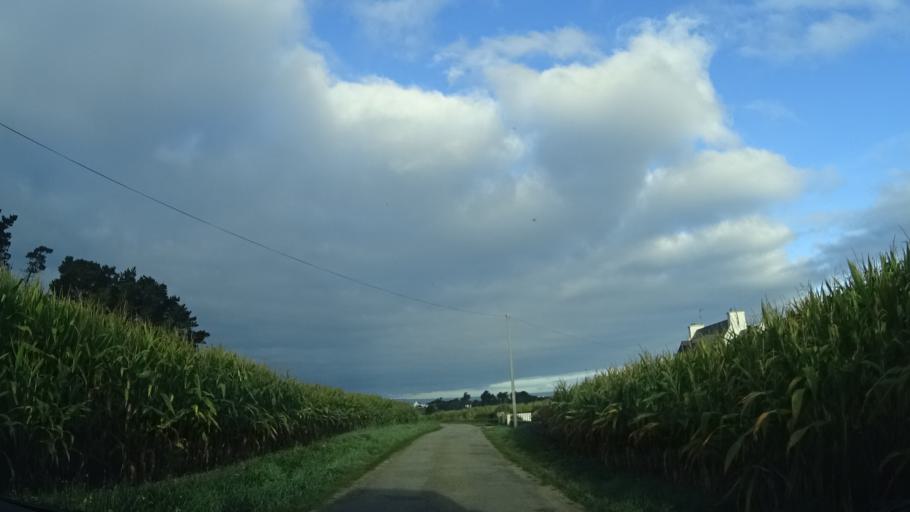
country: FR
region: Brittany
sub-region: Departement du Finistere
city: Lampaul-Plouarzel
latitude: 48.4594
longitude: -4.7531
